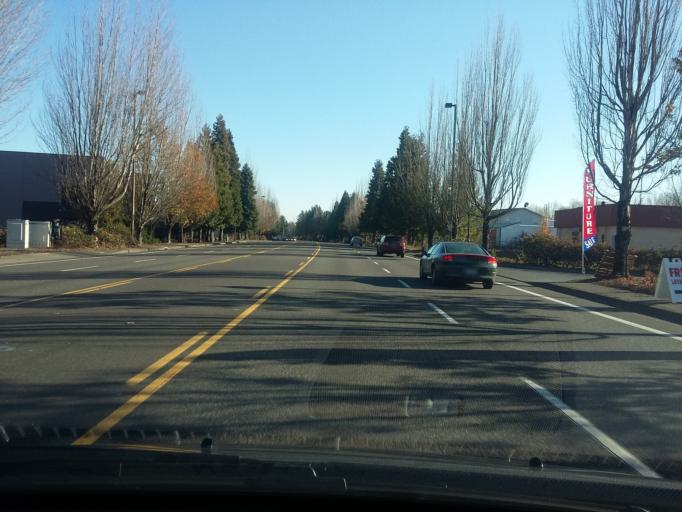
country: US
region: Washington
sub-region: Clark County
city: Mill Plain
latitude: 45.5626
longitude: -122.5268
